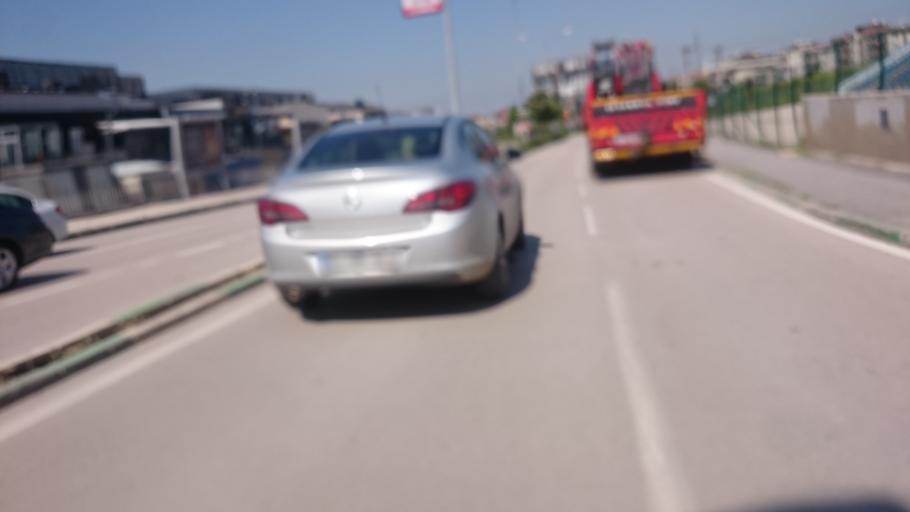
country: TR
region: Bursa
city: Yildirim
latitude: 40.2263
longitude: 28.9718
